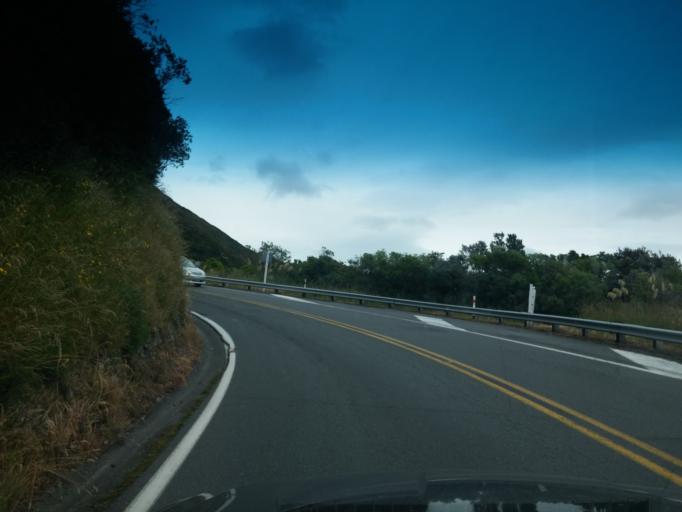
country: NZ
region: Wellington
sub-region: Upper Hutt City
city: Upper Hutt
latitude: -41.1111
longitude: 175.2445
